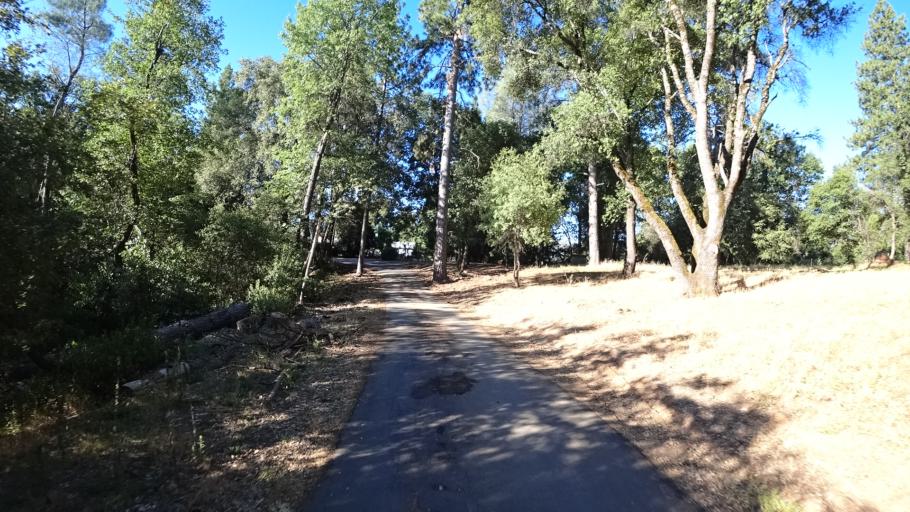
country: US
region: California
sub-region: Amador County
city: Pioneer
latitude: 38.3805
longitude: -120.5709
